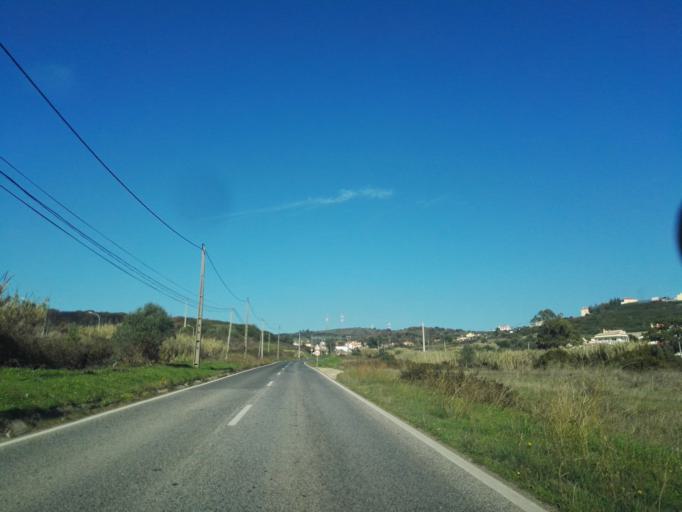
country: PT
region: Lisbon
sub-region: Loures
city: Loures
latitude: 38.8612
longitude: -9.1816
